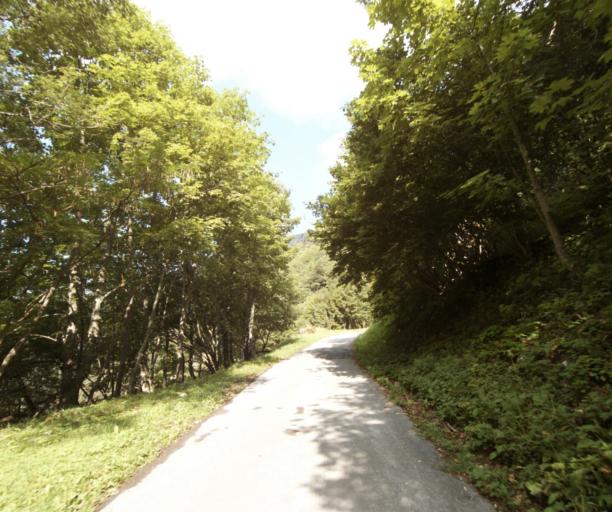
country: CH
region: Vaud
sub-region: Riviera-Pays-d'Enhaut District
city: Caux
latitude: 46.4218
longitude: 6.9853
